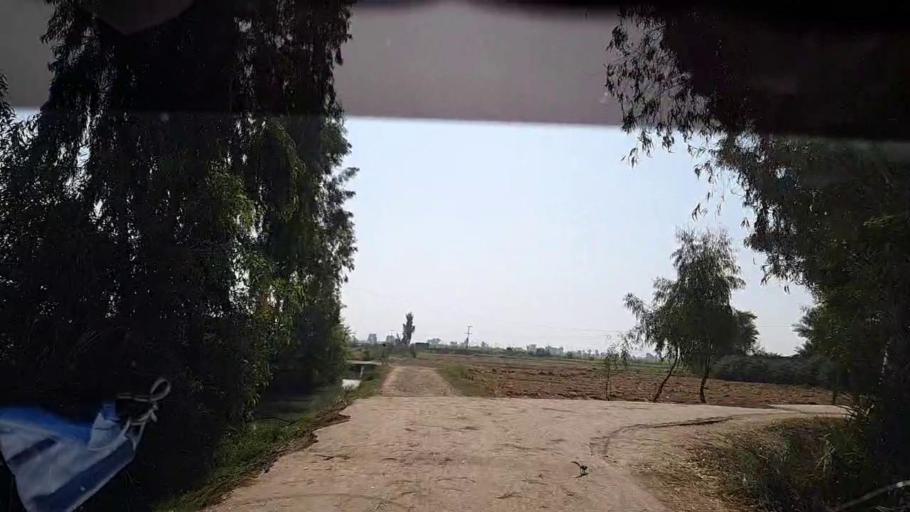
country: PK
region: Sindh
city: Naudero
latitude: 27.6976
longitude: 68.4061
